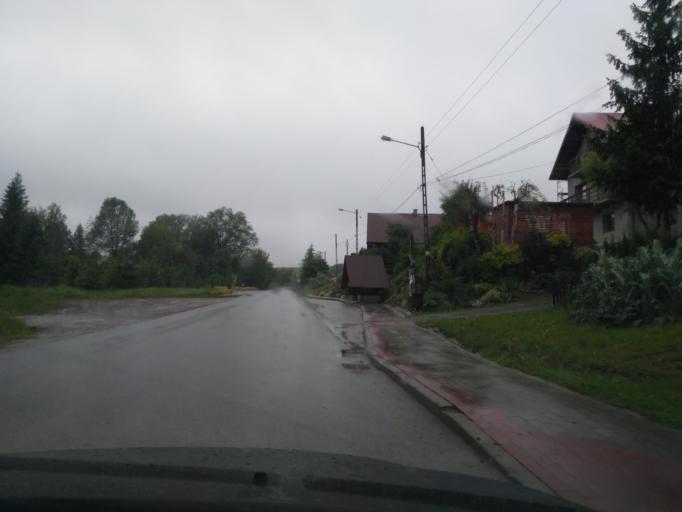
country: PL
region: Lesser Poland Voivodeship
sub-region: Powiat gorlicki
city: Lipinki
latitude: 49.6223
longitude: 21.2632
